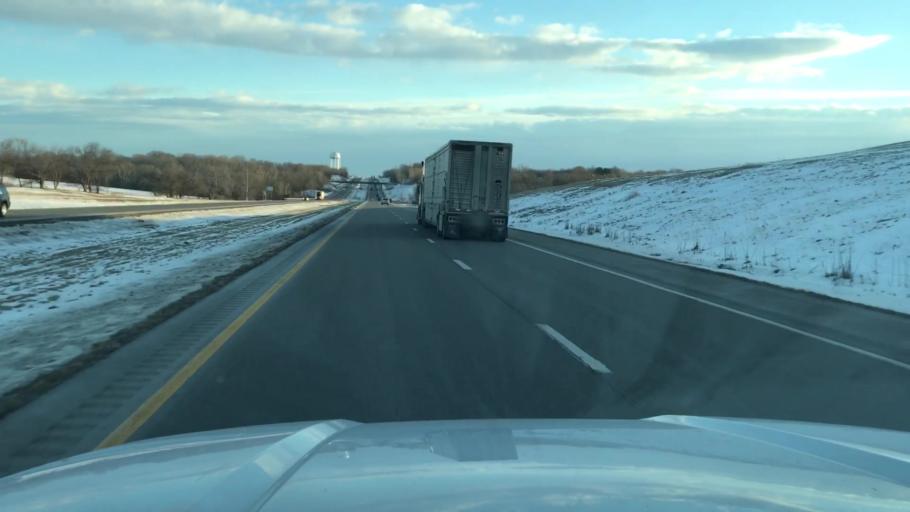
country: US
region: Missouri
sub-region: Andrew County
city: Country Club Village
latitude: 39.8141
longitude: -94.8035
